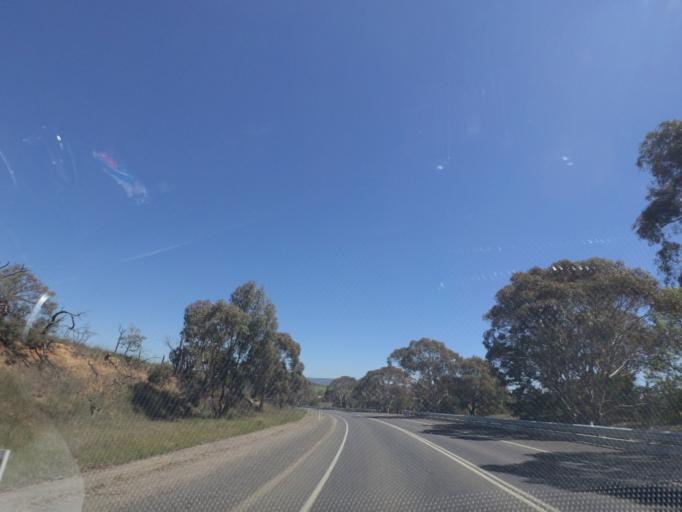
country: AU
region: Victoria
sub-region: Hume
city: Sunbury
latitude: -37.2861
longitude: 144.7852
